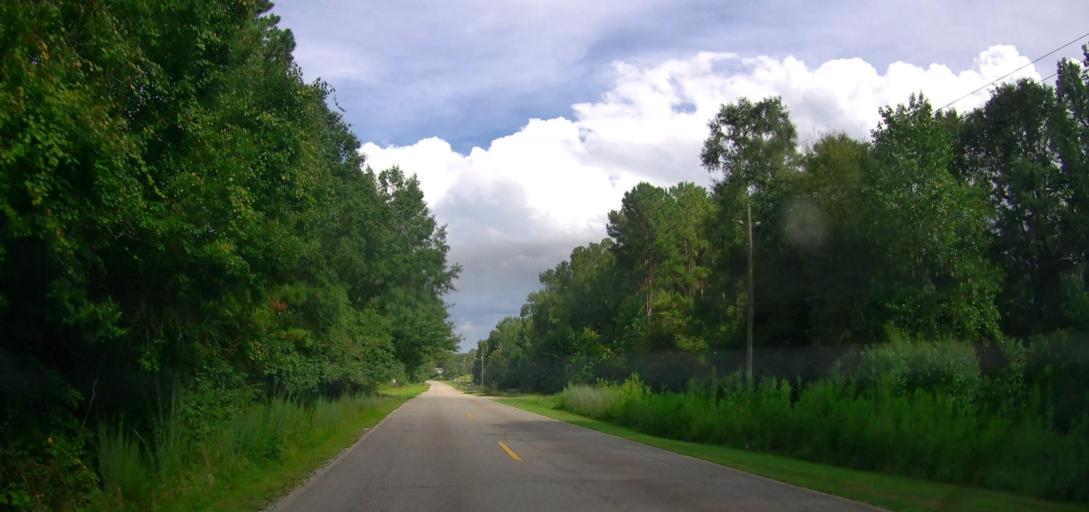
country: US
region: Alabama
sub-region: Russell County
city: Phenix City
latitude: 32.6051
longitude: -84.9577
